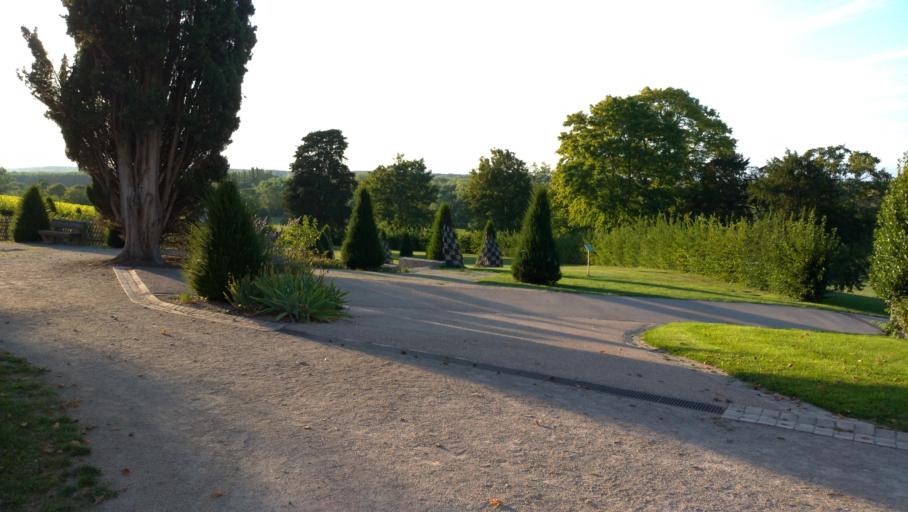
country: FR
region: Pays de la Loire
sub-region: Departement de Maine-et-Loire
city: Villeveque
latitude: 47.5613
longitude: -0.4265
